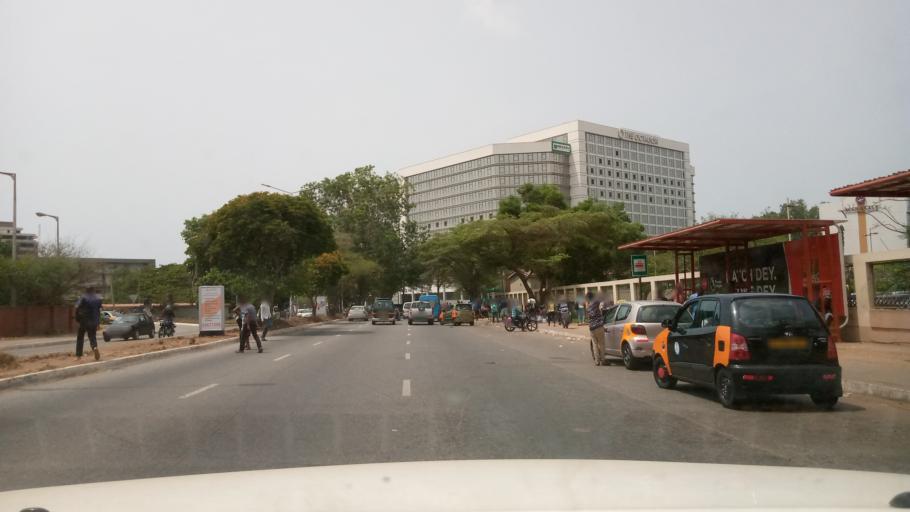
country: GH
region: Greater Accra
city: Accra
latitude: 5.5535
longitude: -0.2018
